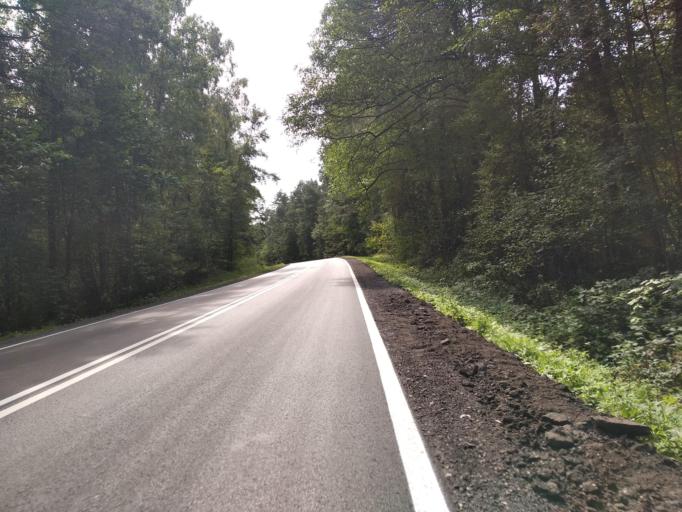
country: PL
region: Subcarpathian Voivodeship
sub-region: Powiat ropczycko-sedziszowski
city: Ostrow
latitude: 50.1334
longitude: 21.5874
